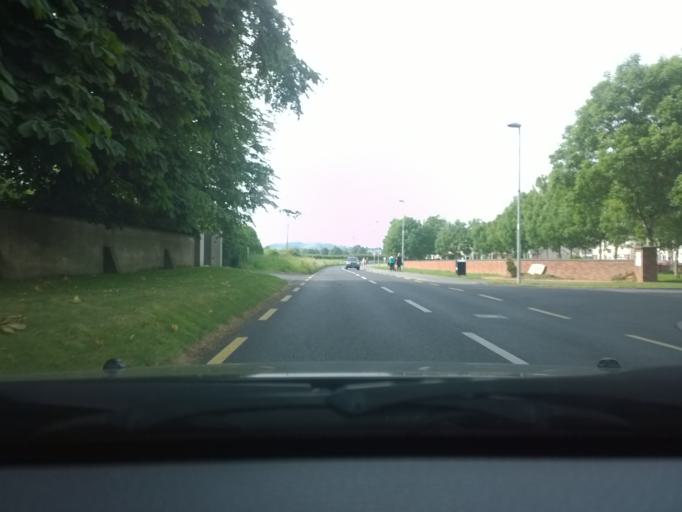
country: IE
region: Leinster
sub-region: Kildare
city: Kildare
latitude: 53.1644
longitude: -6.9127
